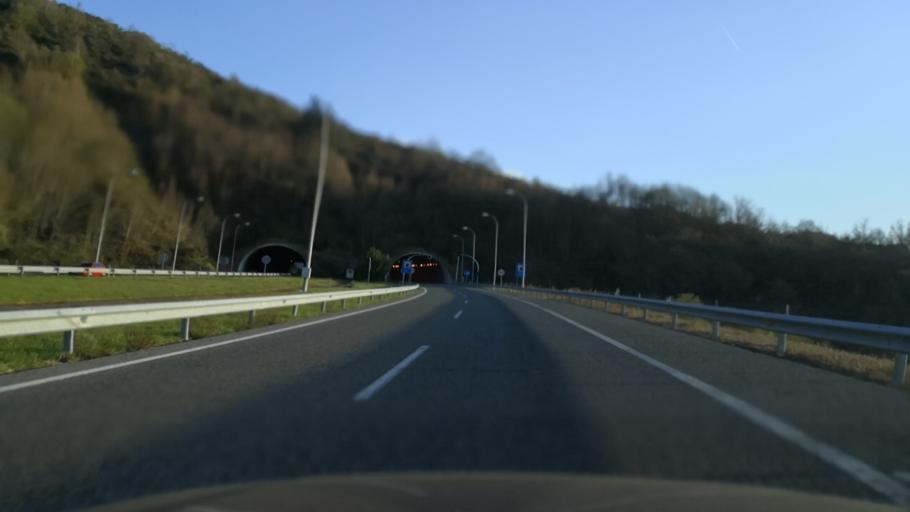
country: ES
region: Galicia
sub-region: Provincia de Lugo
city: Becerrea
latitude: 42.7908
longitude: -7.1098
